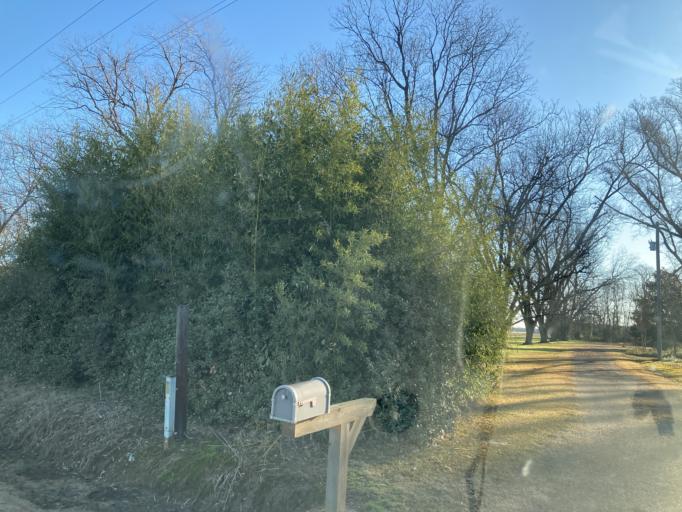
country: US
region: Mississippi
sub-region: Yazoo County
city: Yazoo City
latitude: 32.9272
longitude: -90.5891
